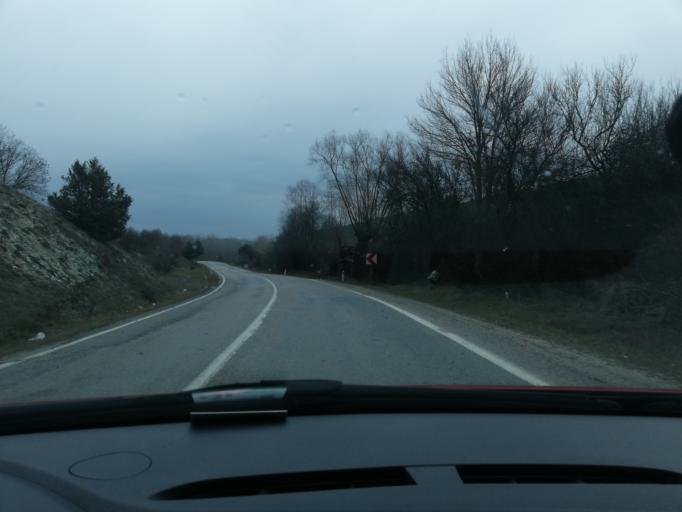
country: TR
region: Kastamonu
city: Daday
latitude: 41.4801
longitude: 33.5698
